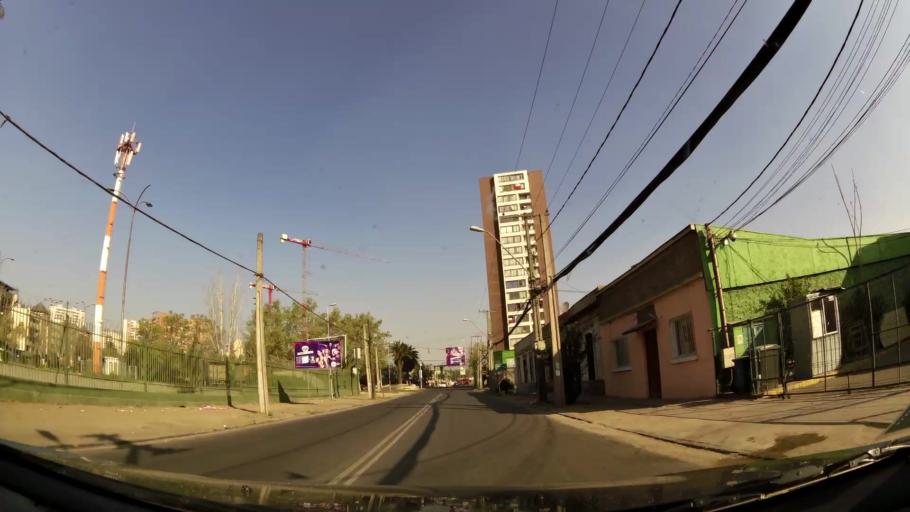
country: CL
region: Santiago Metropolitan
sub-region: Provincia de Santiago
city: Santiago
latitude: -33.4057
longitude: -70.6686
